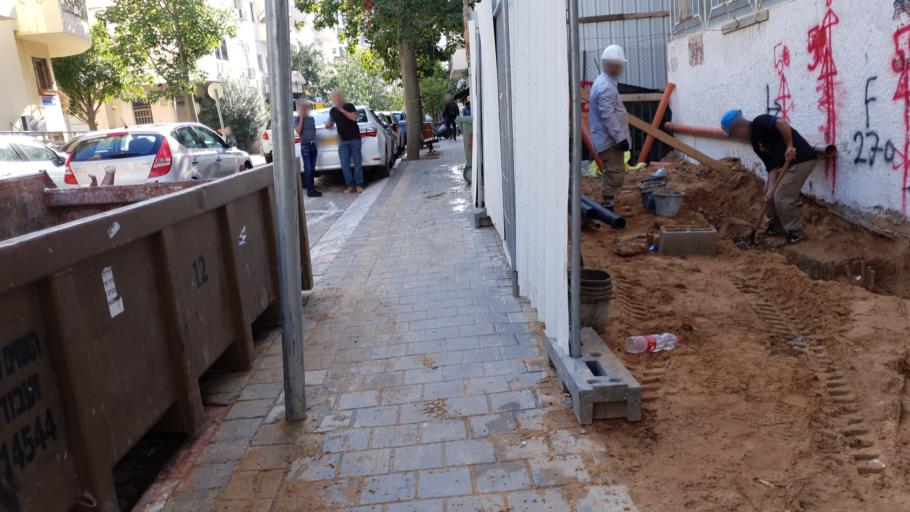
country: IL
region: Tel Aviv
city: Tel Aviv
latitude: 32.0726
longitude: 34.7715
